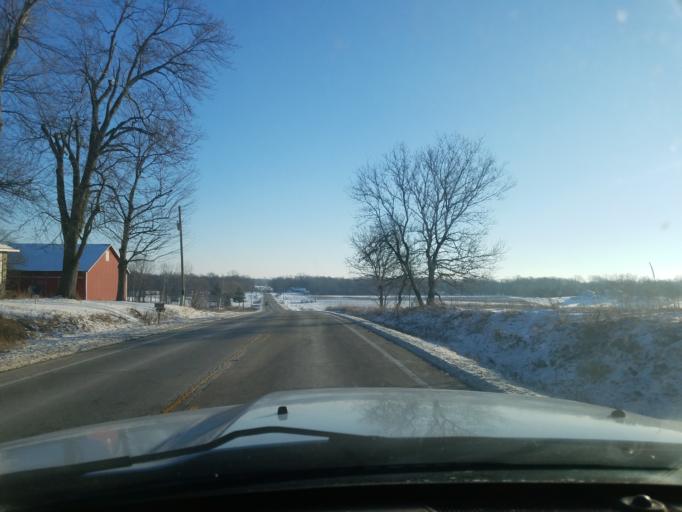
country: US
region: Indiana
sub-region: Noble County
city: Ligonier
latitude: 41.4559
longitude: -85.5348
